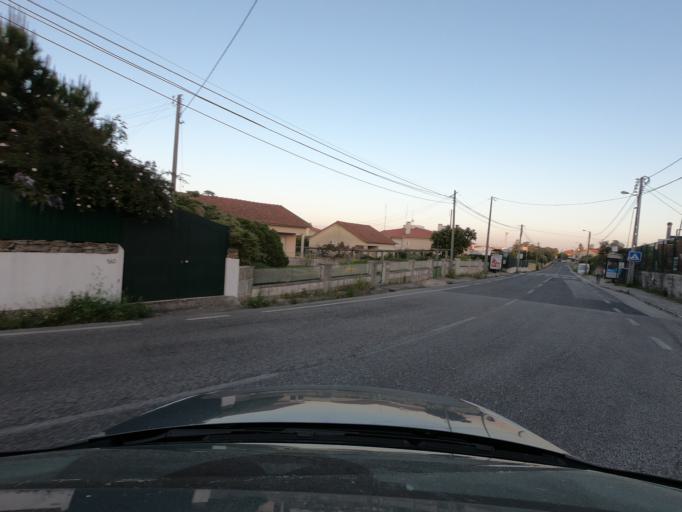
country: PT
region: Lisbon
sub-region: Sintra
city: Rio de Mouro
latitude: 38.7613
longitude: -9.3489
